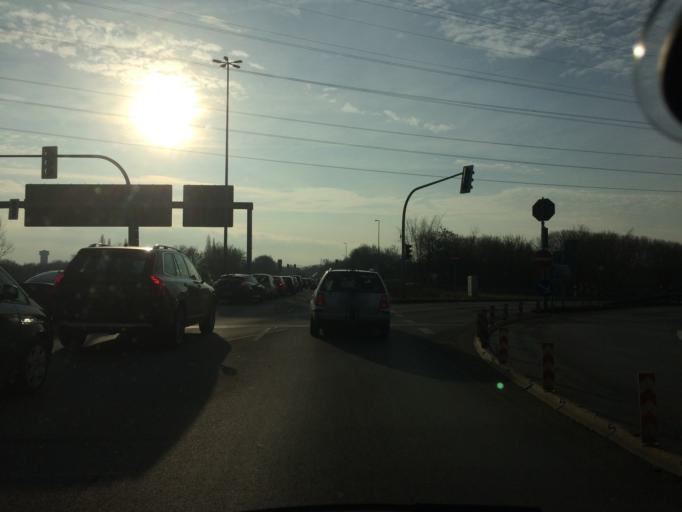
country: DE
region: North Rhine-Westphalia
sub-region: Regierungsbezirk Dusseldorf
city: Oberhausen
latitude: 51.4964
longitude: 6.8637
